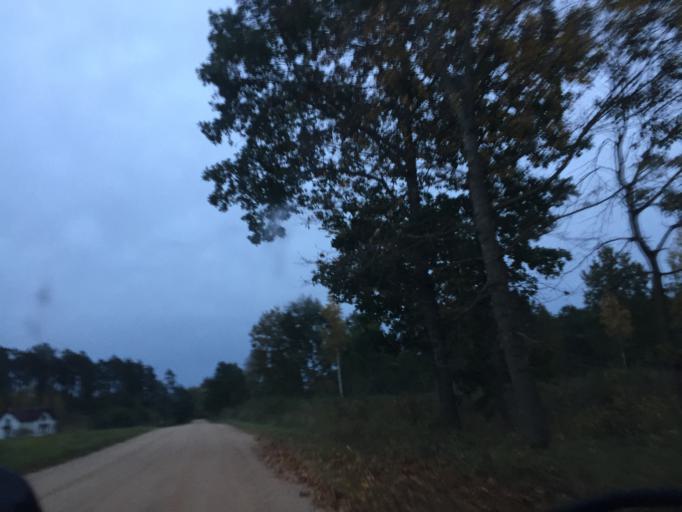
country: LV
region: Adazi
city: Adazi
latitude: 57.0840
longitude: 24.3600
